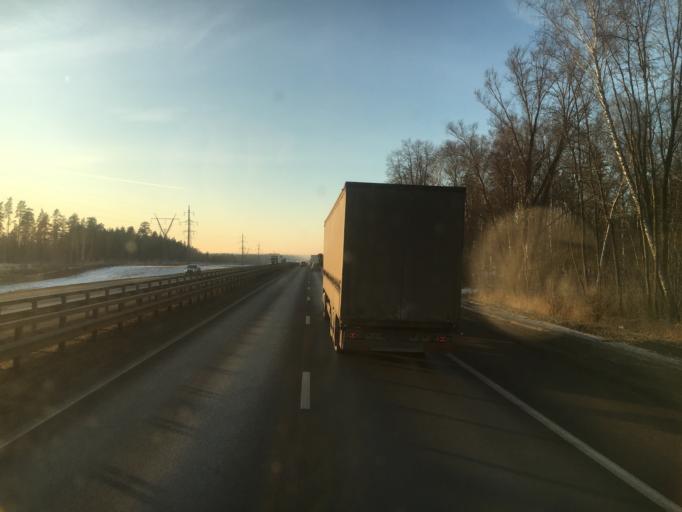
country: RU
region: Samara
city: Povolzhskiy
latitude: 53.5181
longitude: 49.7902
